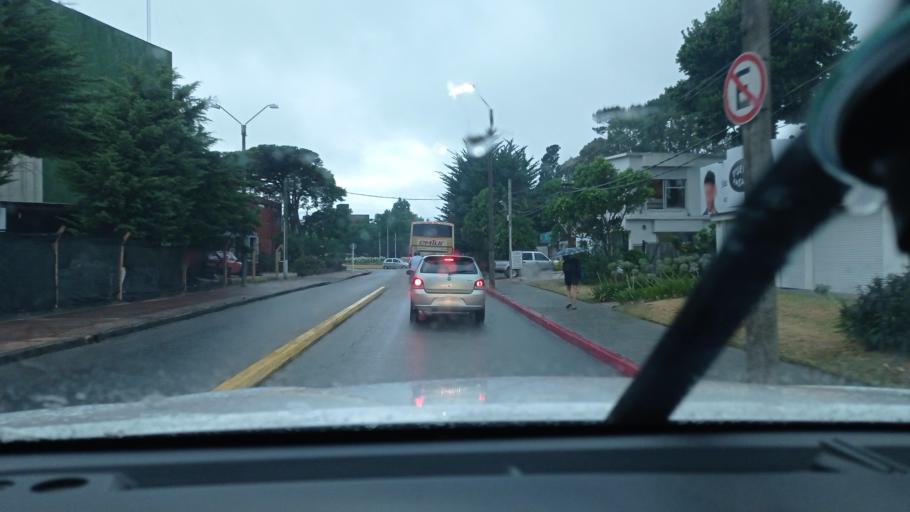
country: UY
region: Maldonado
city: Maldonado
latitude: -34.9150
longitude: -54.9541
